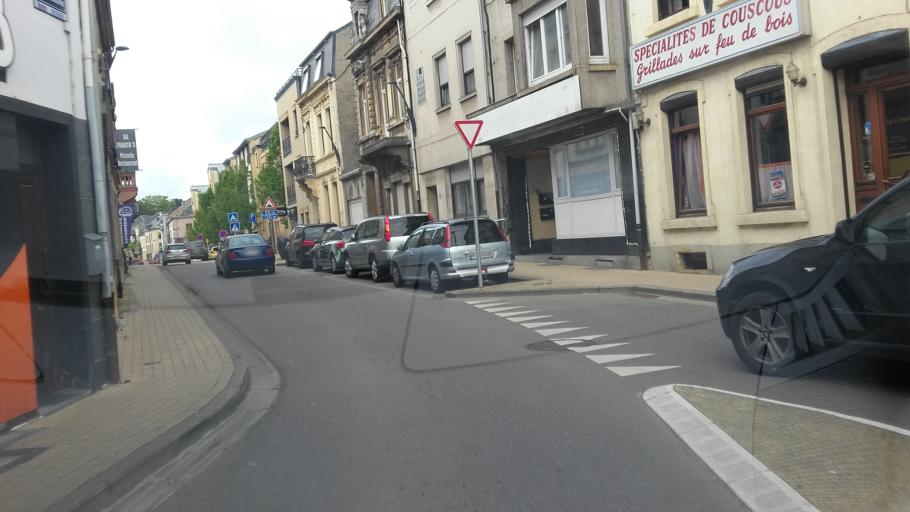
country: BE
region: Wallonia
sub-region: Province du Luxembourg
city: Arlon
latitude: 49.6858
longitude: 5.8146
